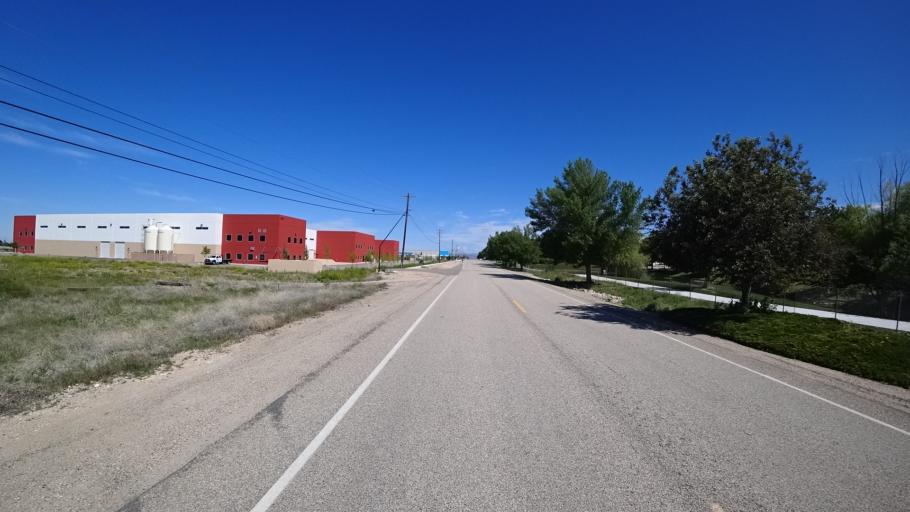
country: US
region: Idaho
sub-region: Ada County
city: Boise
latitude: 43.5239
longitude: -116.1481
